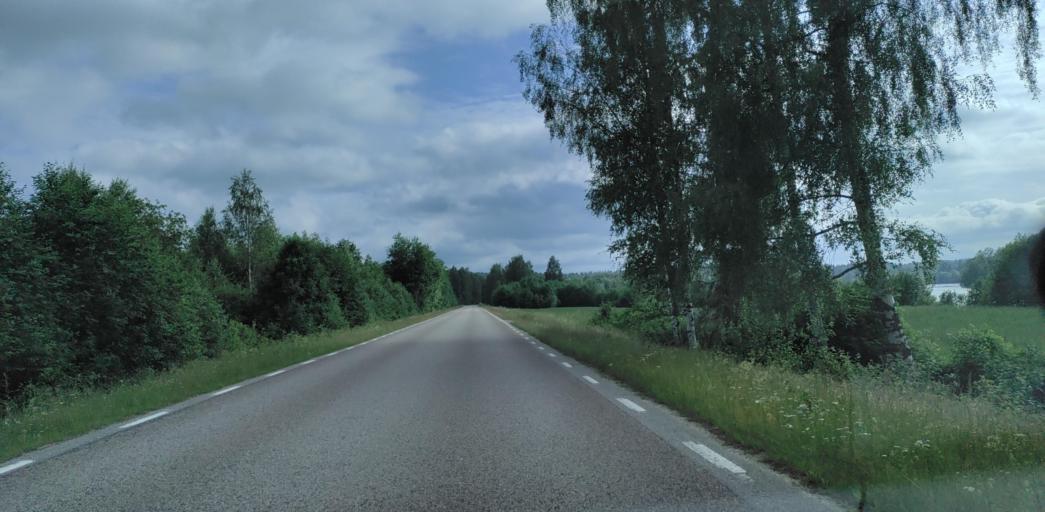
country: SE
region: Vaermland
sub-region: Hagfors Kommun
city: Hagfors
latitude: 60.0687
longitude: 13.5674
